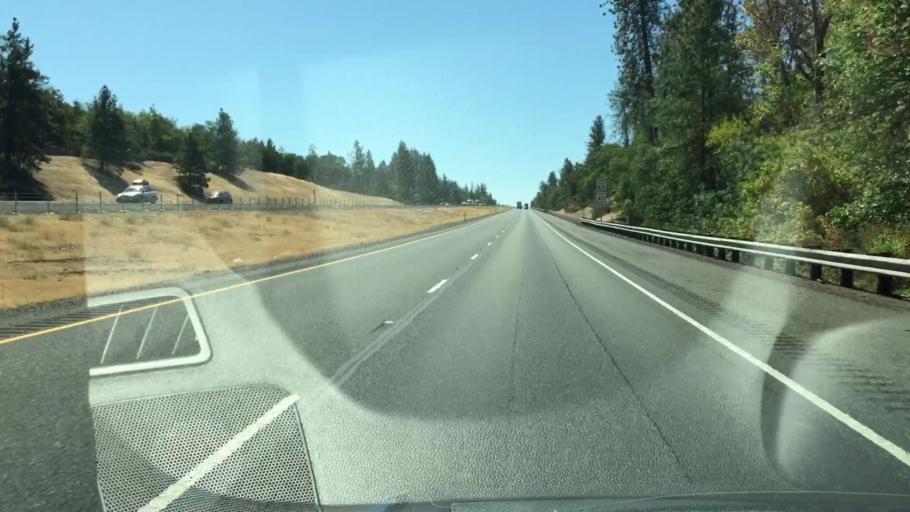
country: US
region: Oregon
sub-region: Josephine County
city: Merlin
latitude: 42.5565
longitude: -123.3717
